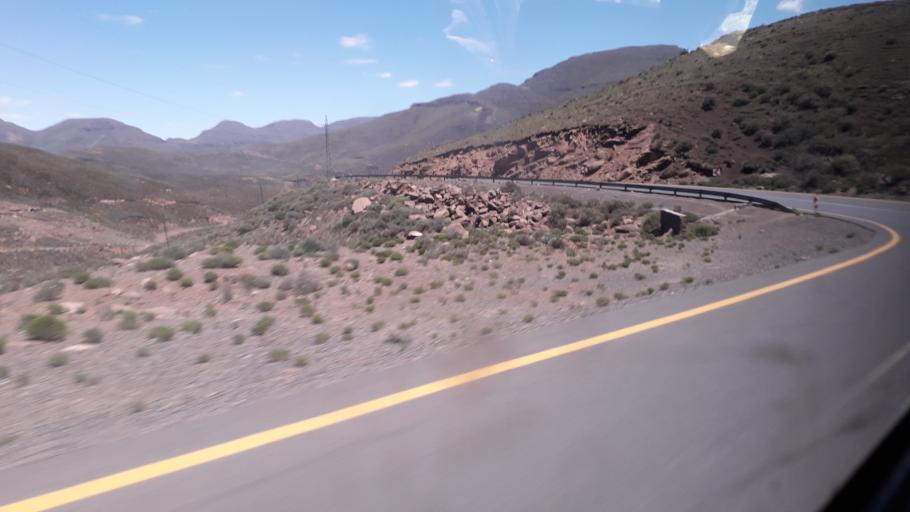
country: ZA
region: Orange Free State
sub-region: Thabo Mofutsanyana District Municipality
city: Phuthaditjhaba
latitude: -28.7697
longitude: 28.6655
